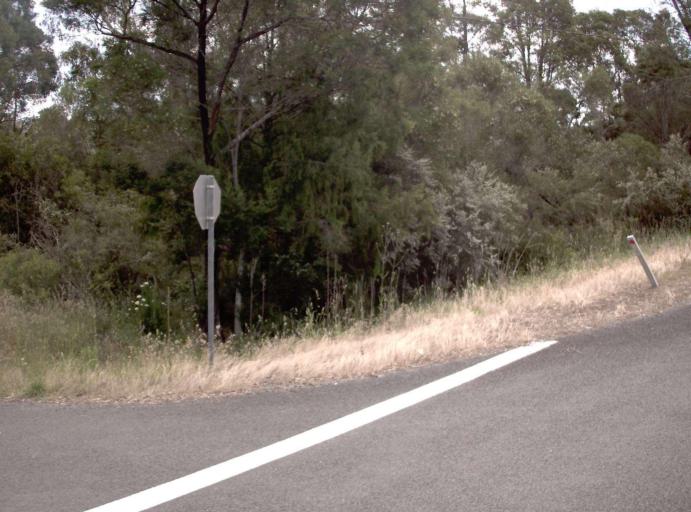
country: AU
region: New South Wales
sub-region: Bega Valley
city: Eden
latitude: -37.4690
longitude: 149.5890
